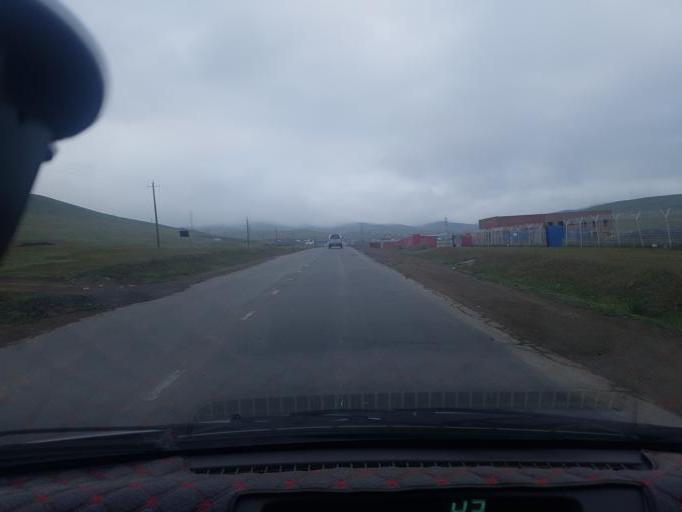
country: MN
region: Ulaanbaatar
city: Ulaanbaatar
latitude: 47.9197
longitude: 106.6264
